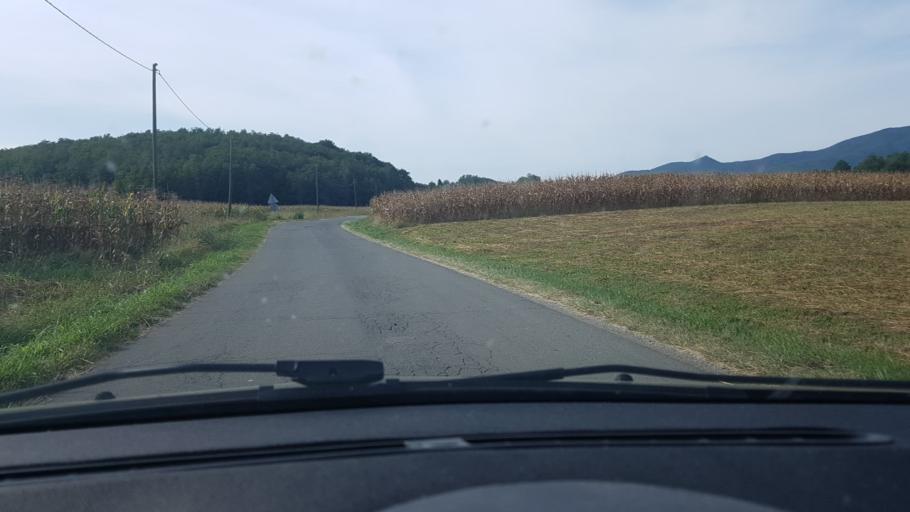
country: HR
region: Krapinsko-Zagorska
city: Zlatar
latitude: 46.1120
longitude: 16.1182
